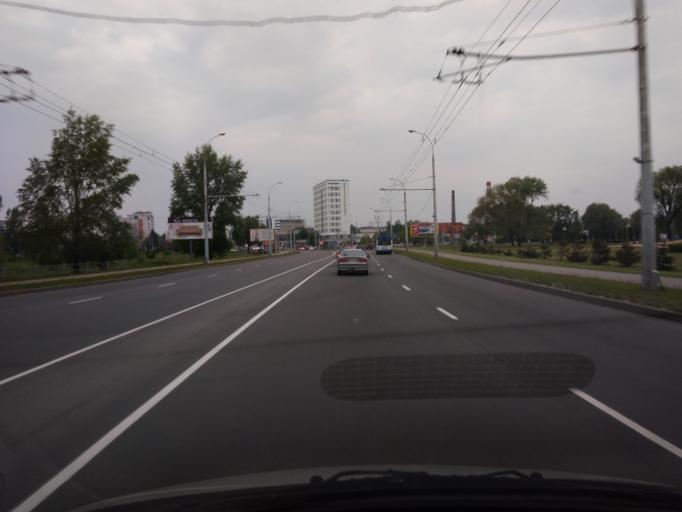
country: BY
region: Brest
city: Brest
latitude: 52.0906
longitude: 23.7331
